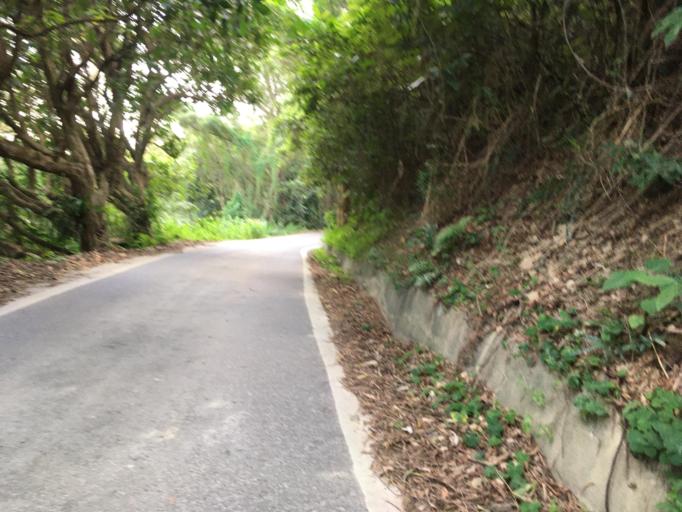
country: TW
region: Taiwan
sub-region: Yilan
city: Yilan
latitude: 24.8403
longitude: 121.7780
